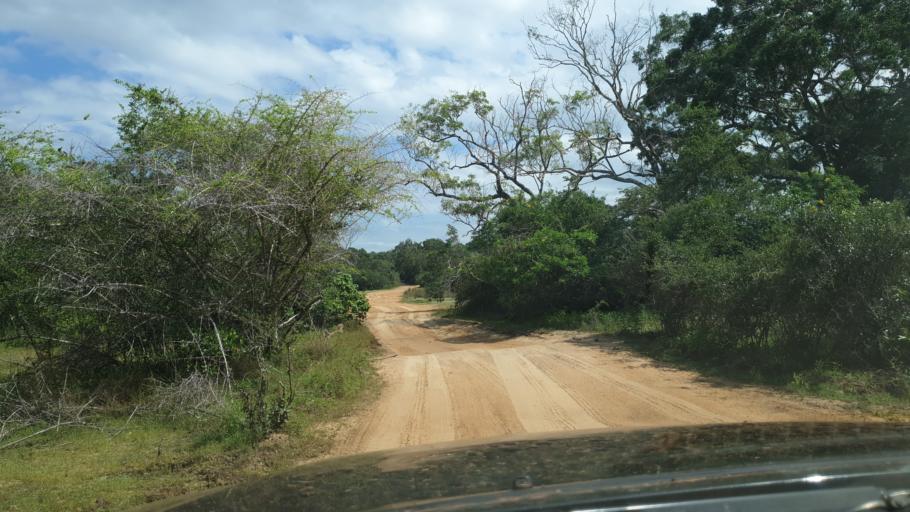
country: LK
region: North Central
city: Anuradhapura
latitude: 8.4212
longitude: 80.0097
